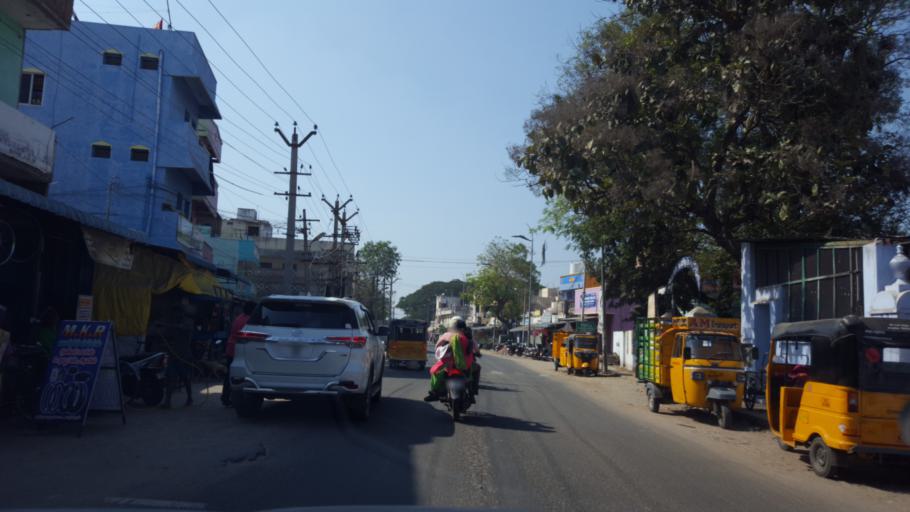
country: IN
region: Tamil Nadu
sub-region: Kancheepuram
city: Kanchipuram
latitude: 12.8508
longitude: 79.6919
